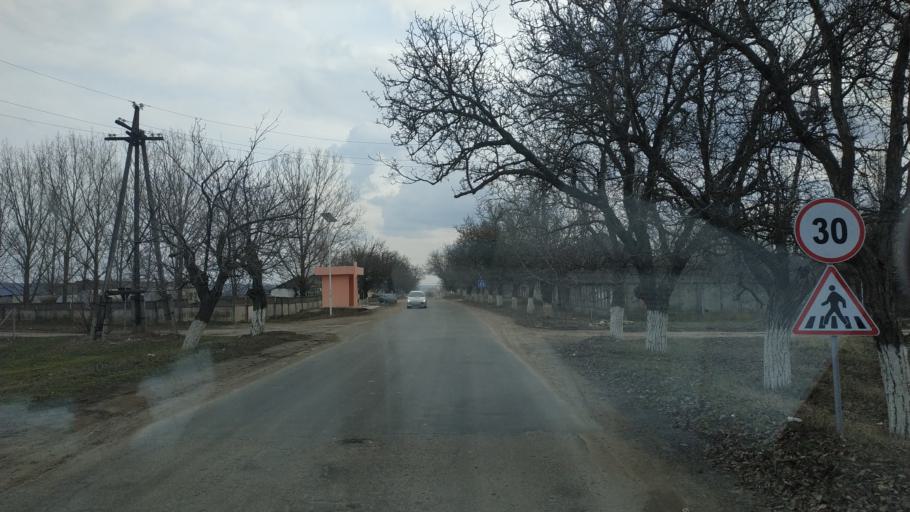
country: MD
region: Anenii Noi
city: Varnita
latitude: 46.8527
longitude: 29.3507
